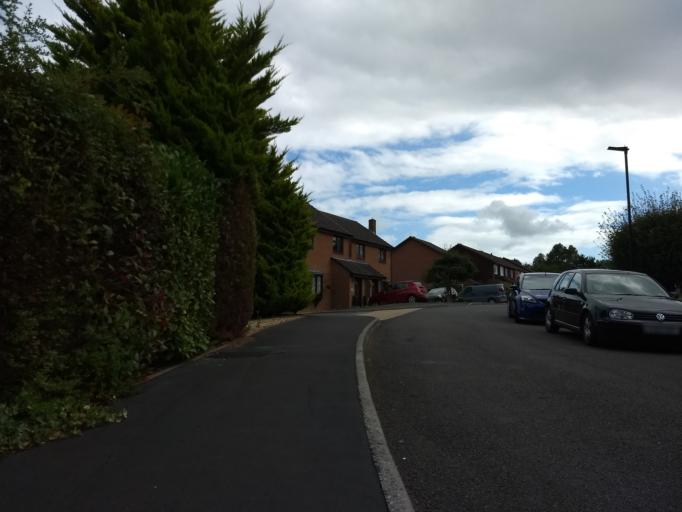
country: GB
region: England
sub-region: Isle of Wight
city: Newport
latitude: 50.7026
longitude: -1.3028
